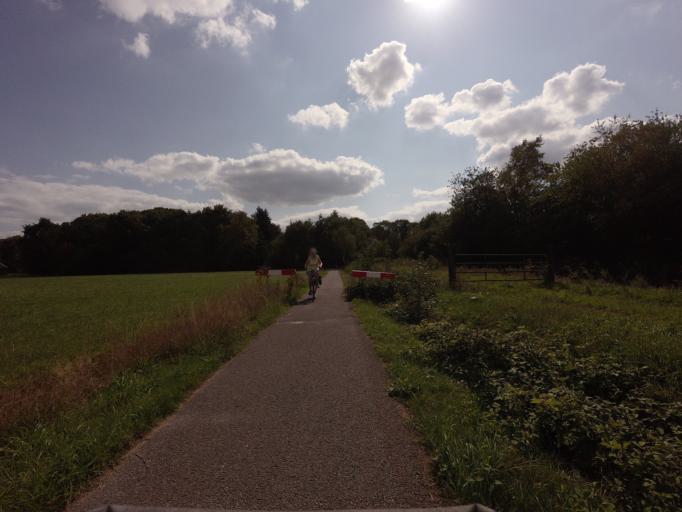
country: NL
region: Drenthe
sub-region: Gemeente Westerveld
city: Dwingeloo
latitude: 52.8397
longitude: 6.4680
